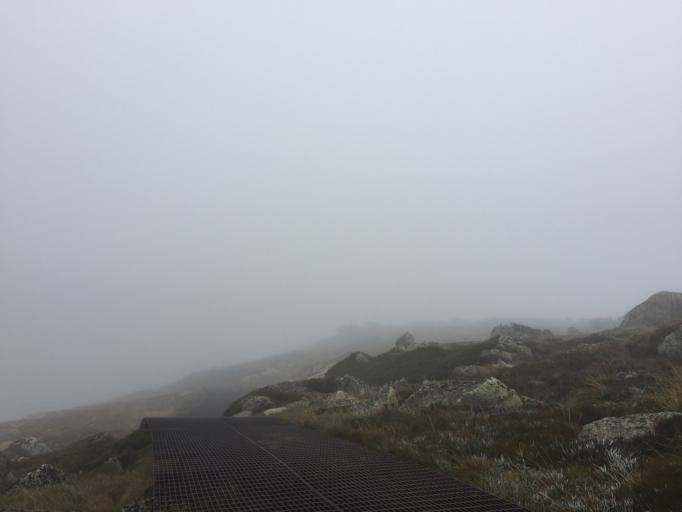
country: AU
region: New South Wales
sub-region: Snowy River
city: Jindabyne
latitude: -36.4651
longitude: 148.2697
